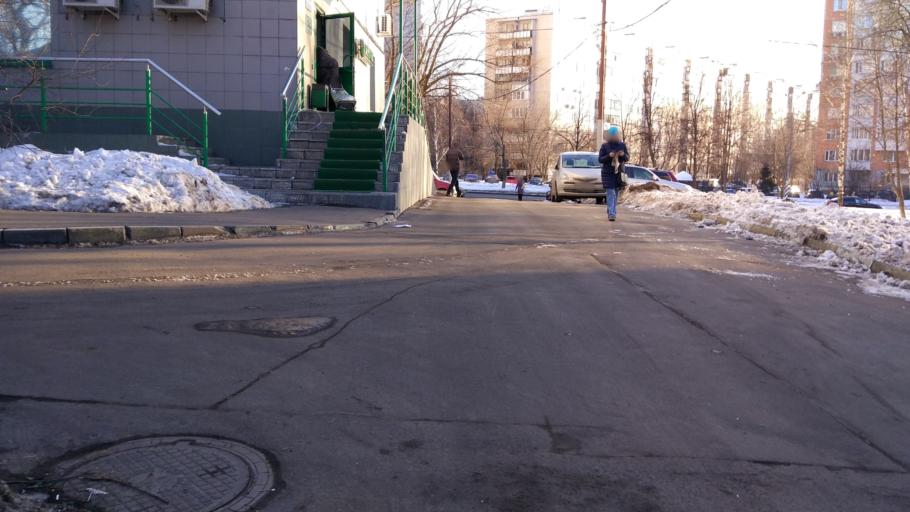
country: RU
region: Moscow
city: Orekhovo-Borisovo Severnoye
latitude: 55.6182
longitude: 37.6999
